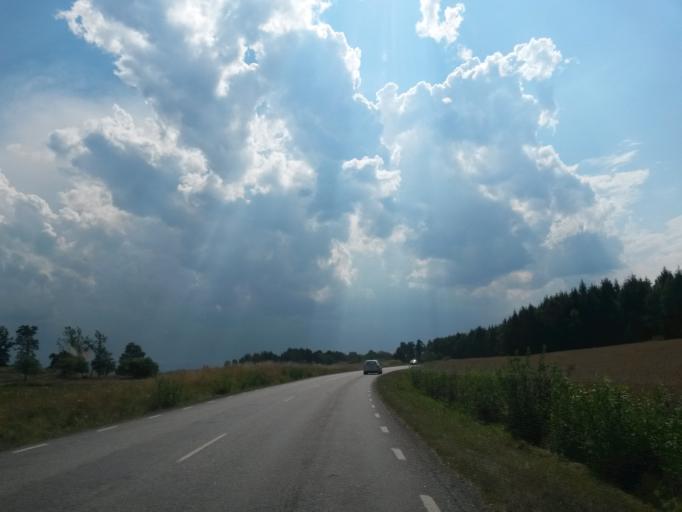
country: SE
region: Vaestra Goetaland
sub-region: Lidkopings Kommun
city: Lidkoping
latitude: 58.6410
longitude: 13.1454
